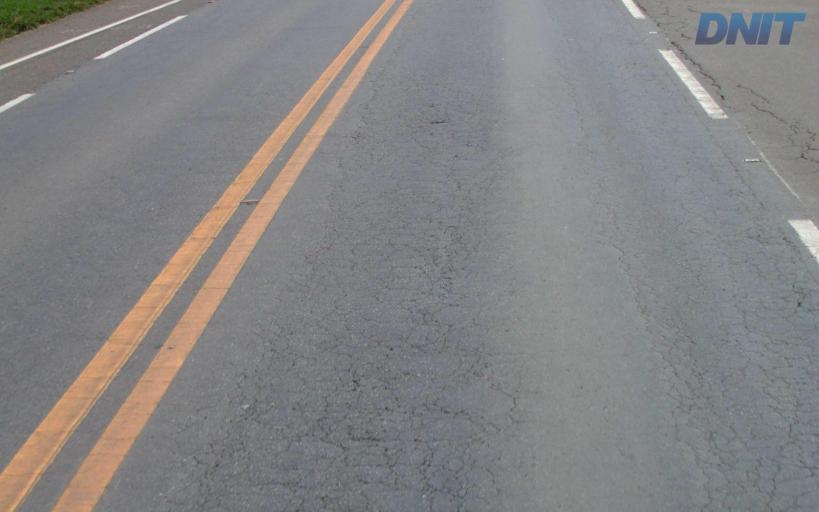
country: BR
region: Minas Gerais
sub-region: Governador Valadares
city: Governador Valadares
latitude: -19.0132
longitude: -42.1400
